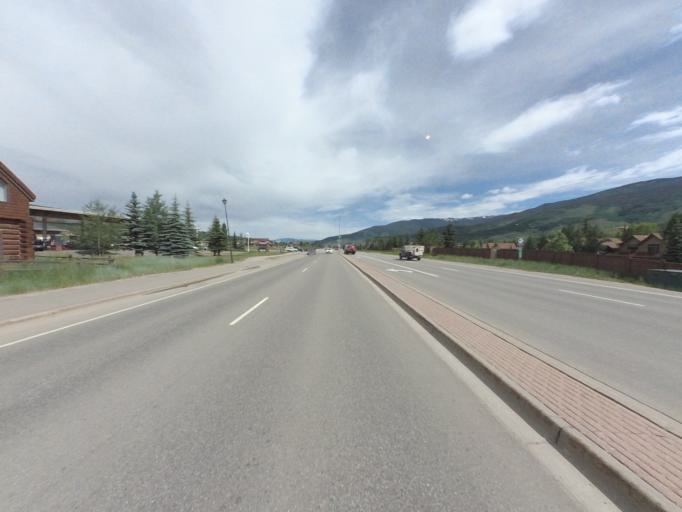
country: US
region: Colorado
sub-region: Summit County
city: Silverthorne
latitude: 39.6459
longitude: -106.0788
